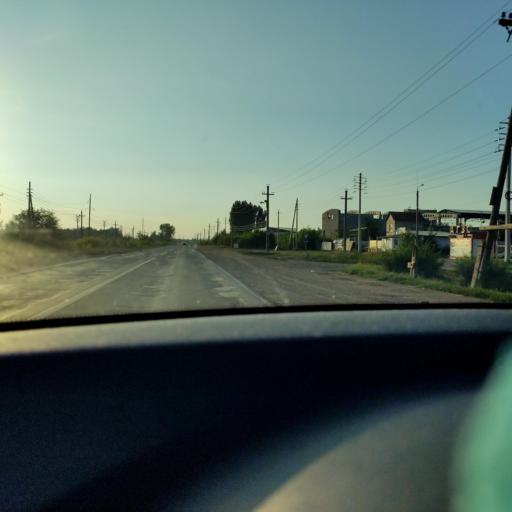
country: RU
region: Samara
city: Kinel'
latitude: 53.2316
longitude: 50.5887
